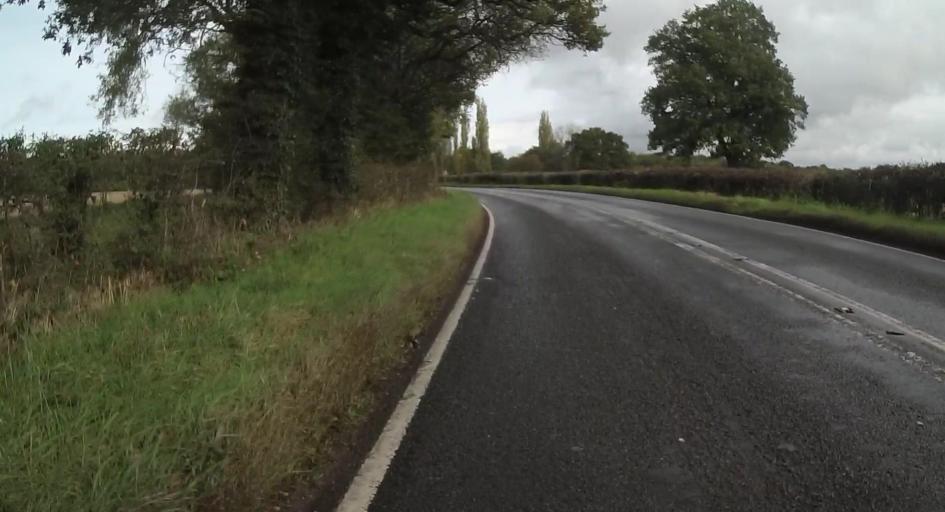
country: GB
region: England
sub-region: Hampshire
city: Odiham
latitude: 51.2768
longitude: -0.9194
